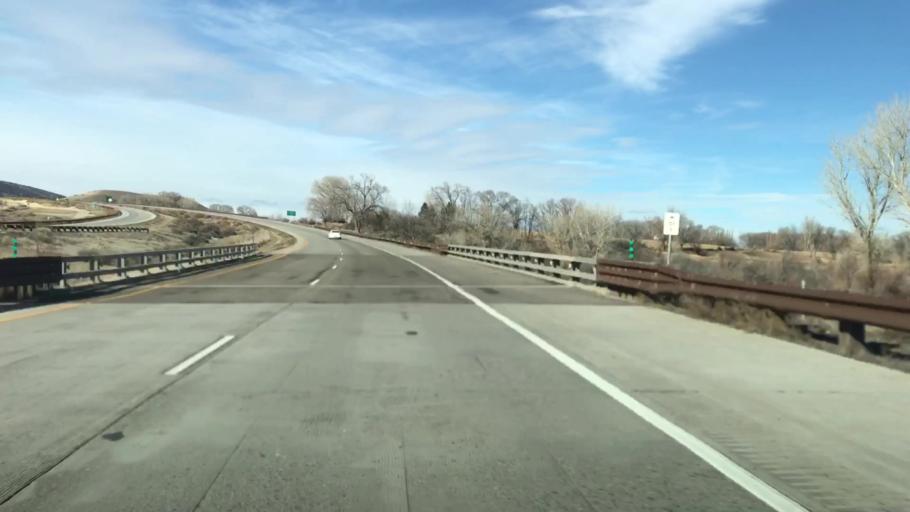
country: US
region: Colorado
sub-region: Mesa County
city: Loma
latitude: 39.1756
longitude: -108.8003
